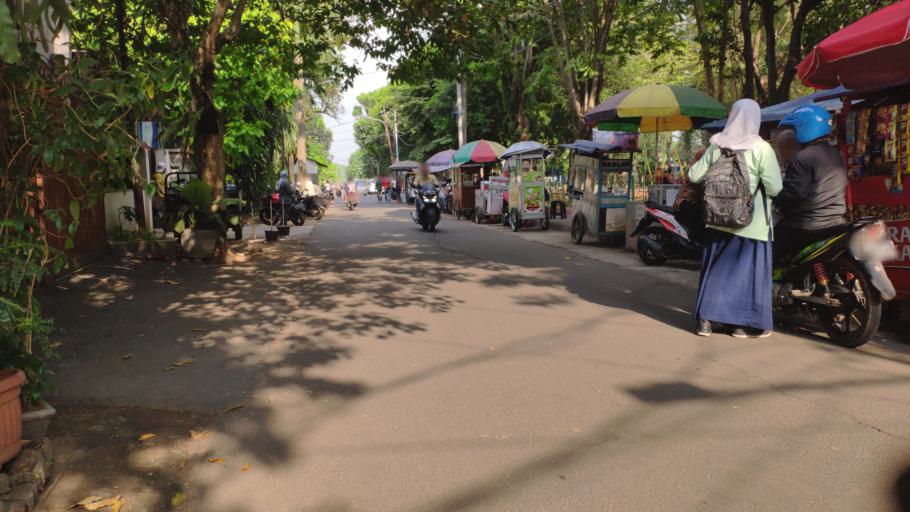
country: ID
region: West Java
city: Pamulang
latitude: -6.3025
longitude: 106.8006
